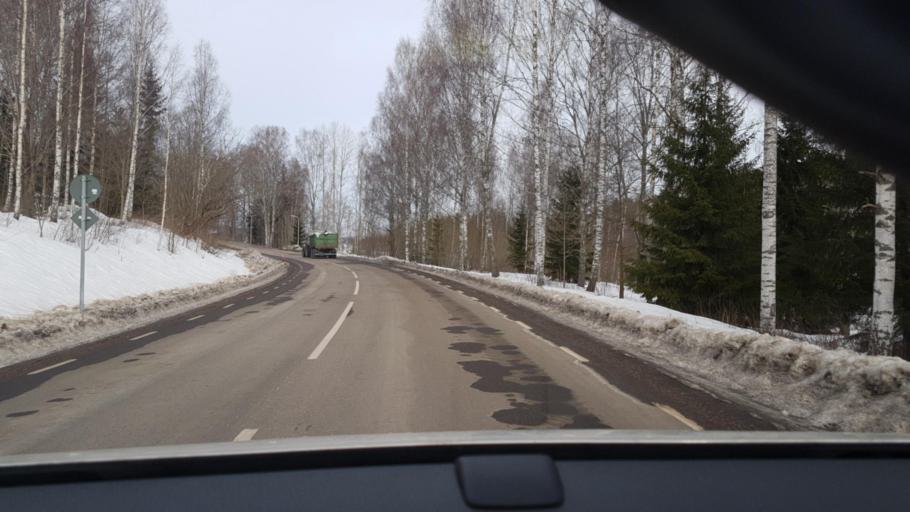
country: SE
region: Vaermland
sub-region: Eda Kommun
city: Amotfors
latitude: 59.7131
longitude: 12.4375
